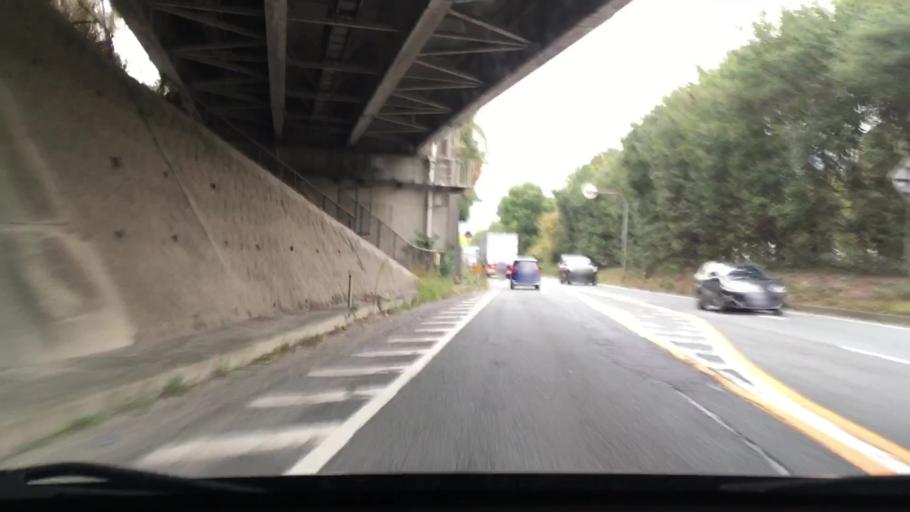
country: JP
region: Yamaguchi
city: Hofu
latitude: 34.0586
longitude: 131.6143
